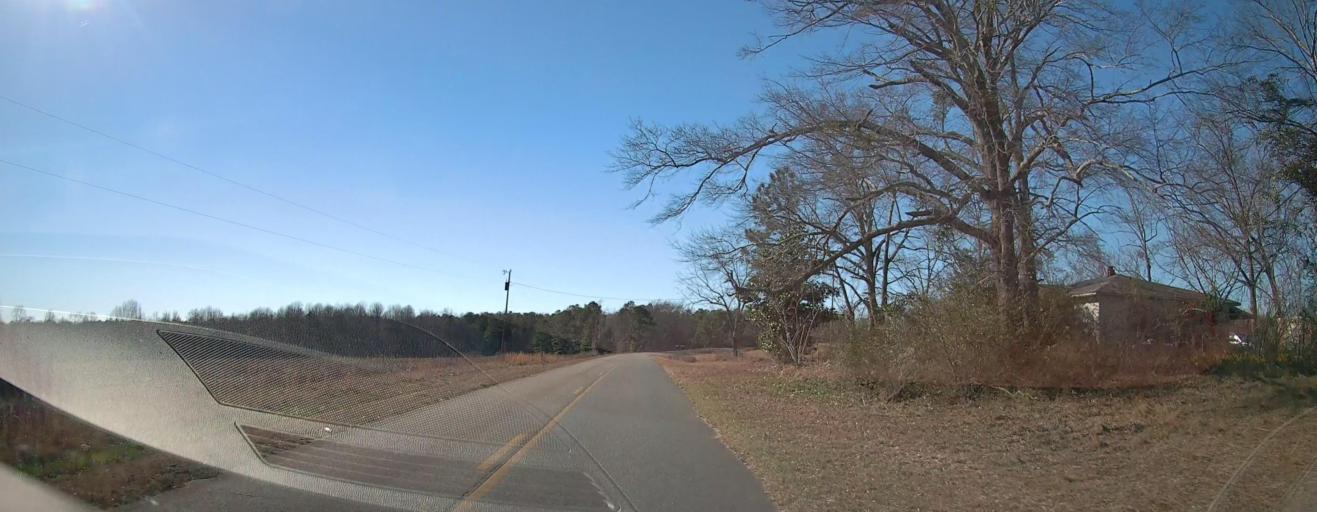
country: US
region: Georgia
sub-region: Taylor County
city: Butler
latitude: 32.6437
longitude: -84.3114
